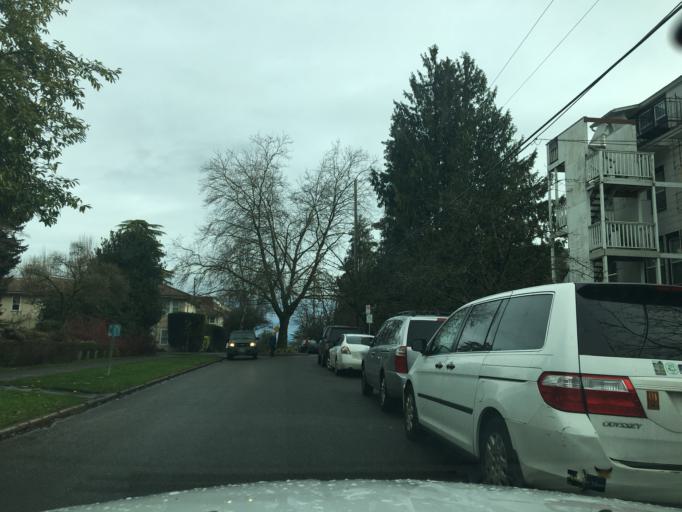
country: US
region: Washington
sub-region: King County
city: Seattle
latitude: 47.6185
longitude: -122.3108
